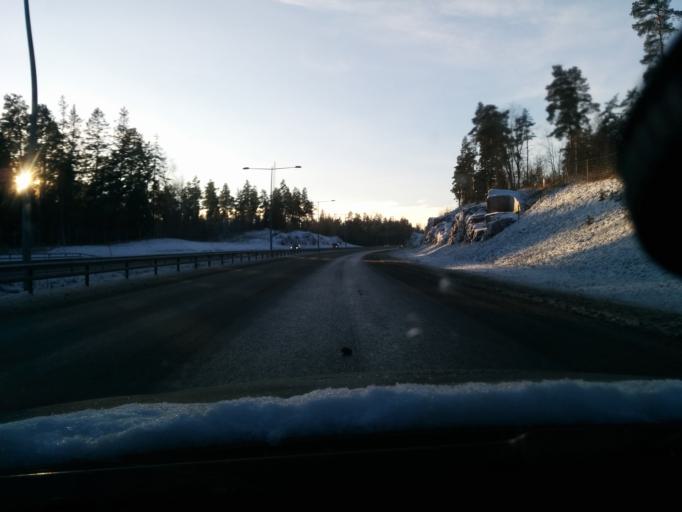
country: SE
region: Stockholm
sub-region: Sollentuna Kommun
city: Sollentuna
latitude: 59.4696
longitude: 17.9829
